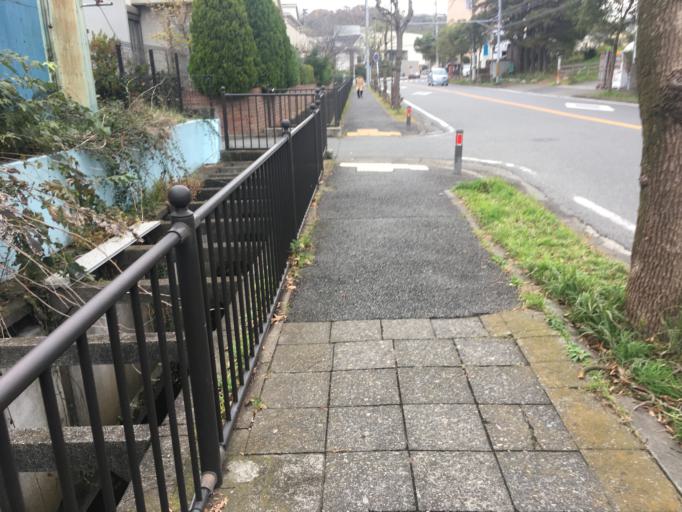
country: JP
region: Kanagawa
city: Kamakura
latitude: 35.3274
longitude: 139.5248
